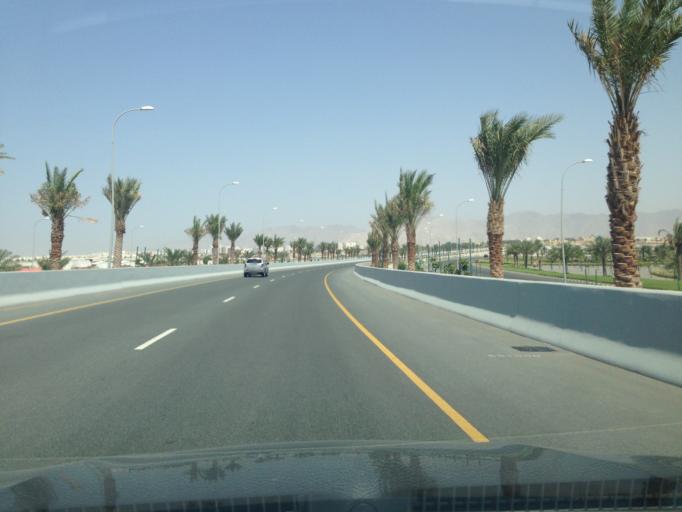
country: OM
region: Muhafazat Masqat
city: Bawshar
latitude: 23.5975
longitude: 58.3316
